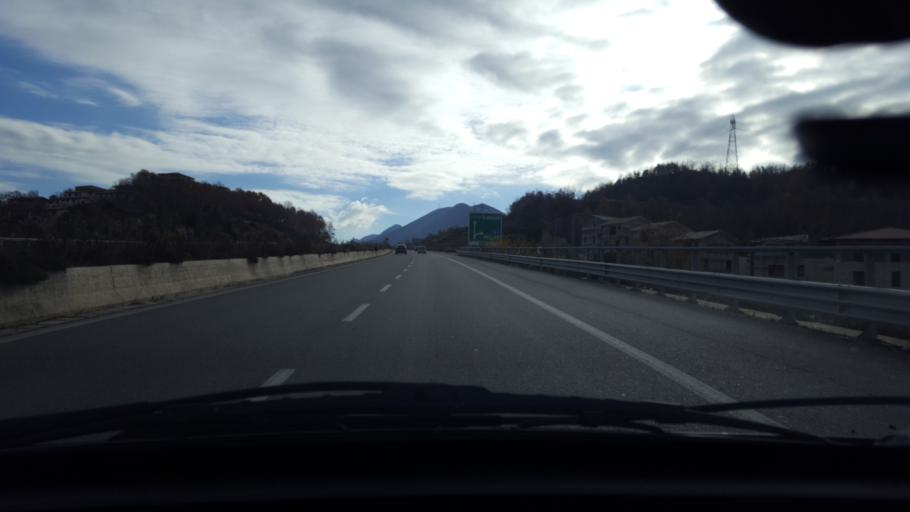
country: AL
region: Tirane
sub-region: Rrethi i Tiranes
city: Petrele
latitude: 41.2733
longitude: 19.8585
